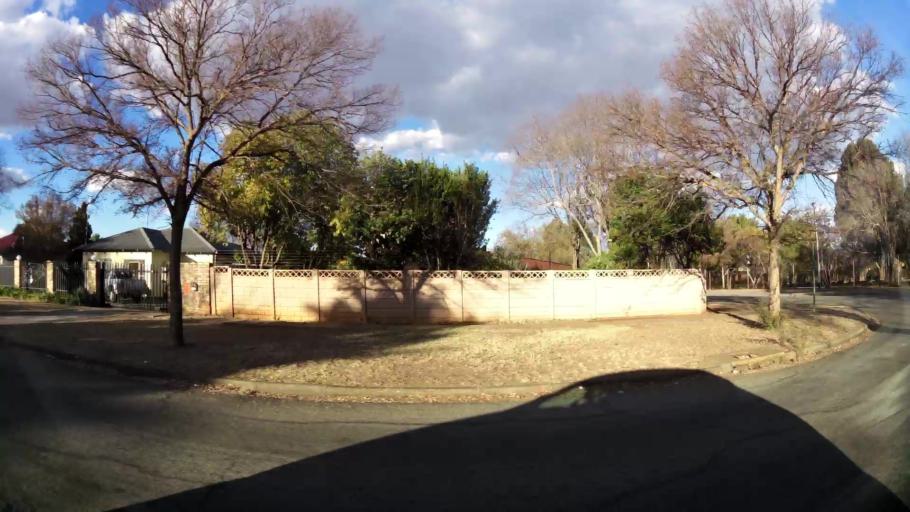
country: ZA
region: North-West
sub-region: Dr Kenneth Kaunda District Municipality
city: Potchefstroom
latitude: -26.7393
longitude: 27.0888
